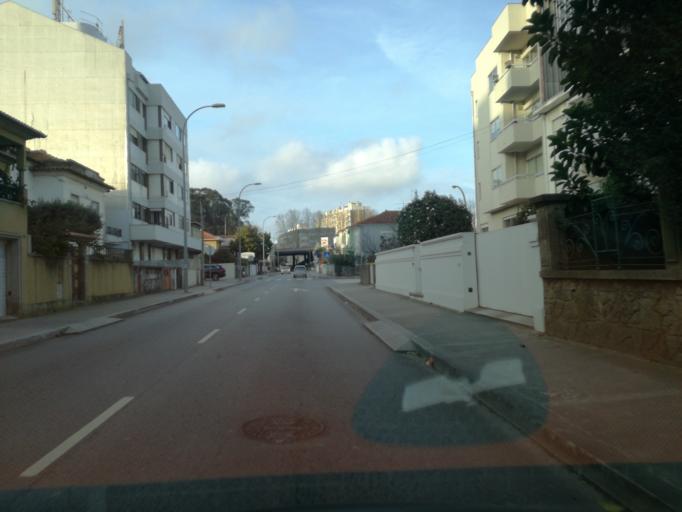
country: PT
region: Porto
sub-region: Porto
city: Porto
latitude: 41.1712
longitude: -8.6260
